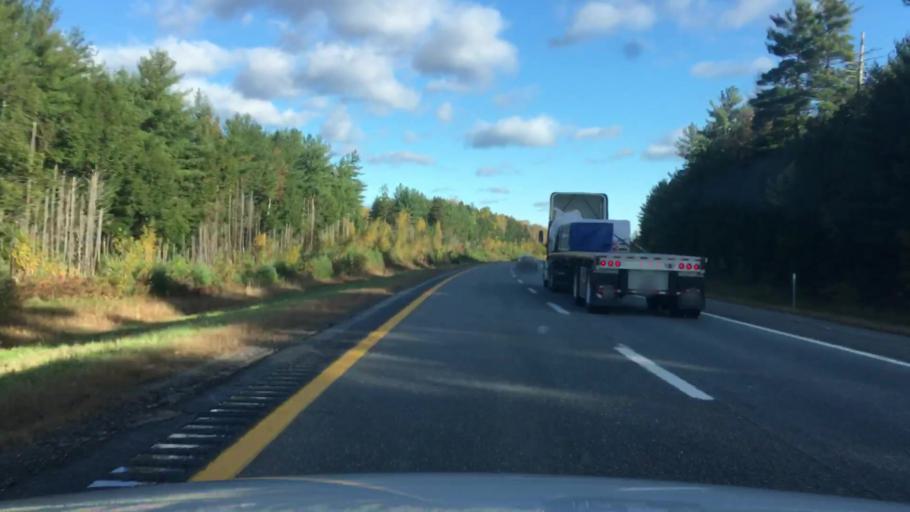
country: US
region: Maine
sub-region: Penobscot County
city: Greenbush
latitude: 45.1505
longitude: -68.7038
